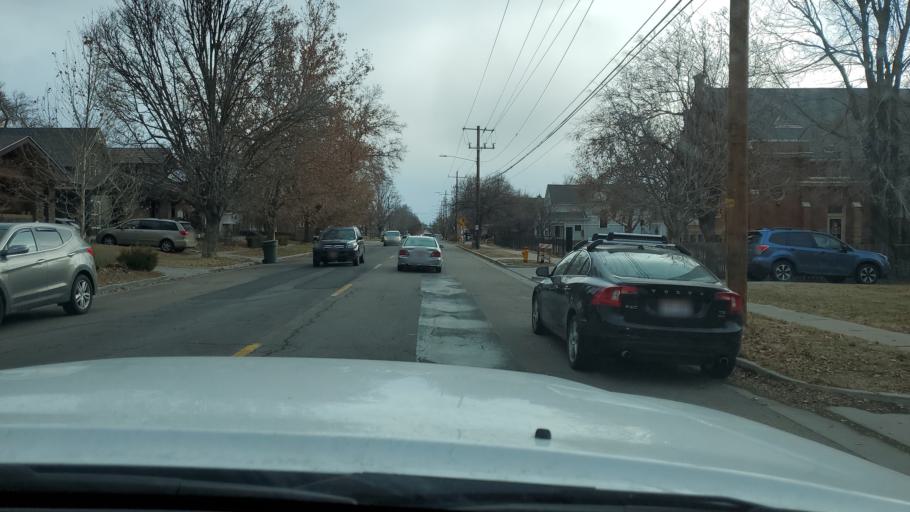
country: US
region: Utah
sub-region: Salt Lake County
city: Salt Lake City
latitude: 40.7448
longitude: -111.8653
